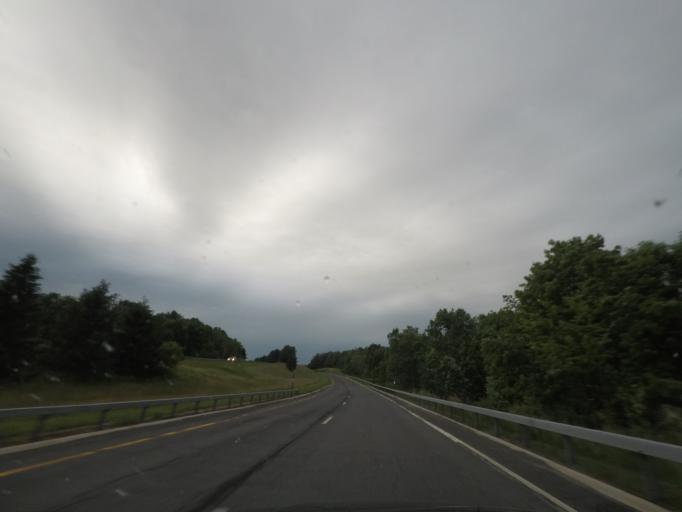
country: US
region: New York
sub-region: Columbia County
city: Chatham
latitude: 42.3332
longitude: -73.5677
